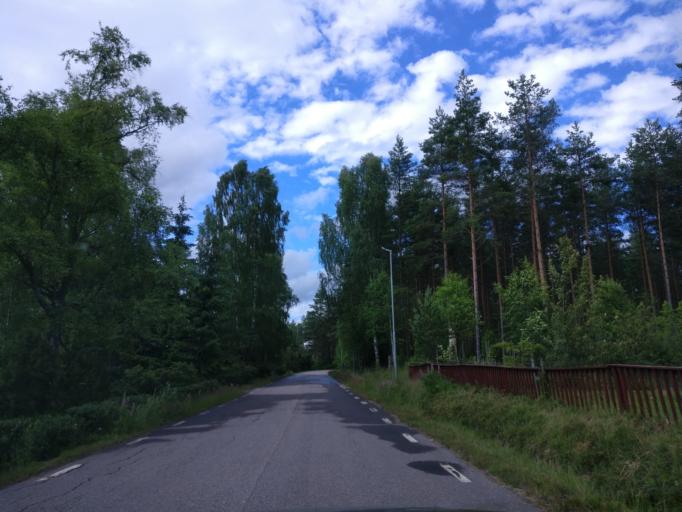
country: SE
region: Vaermland
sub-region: Munkfors Kommun
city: Munkfors
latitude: 59.9751
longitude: 13.4853
